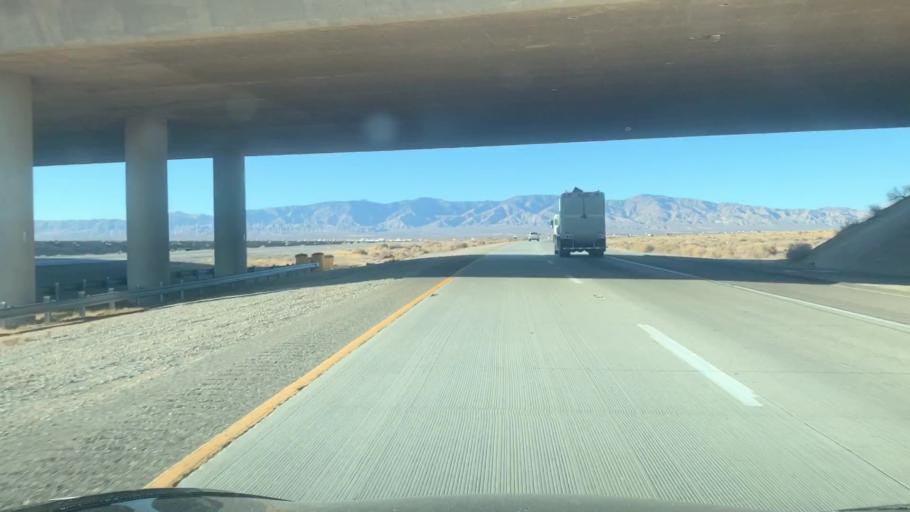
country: US
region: California
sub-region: Kern County
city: Mojave
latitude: 35.0379
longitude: -118.1068
